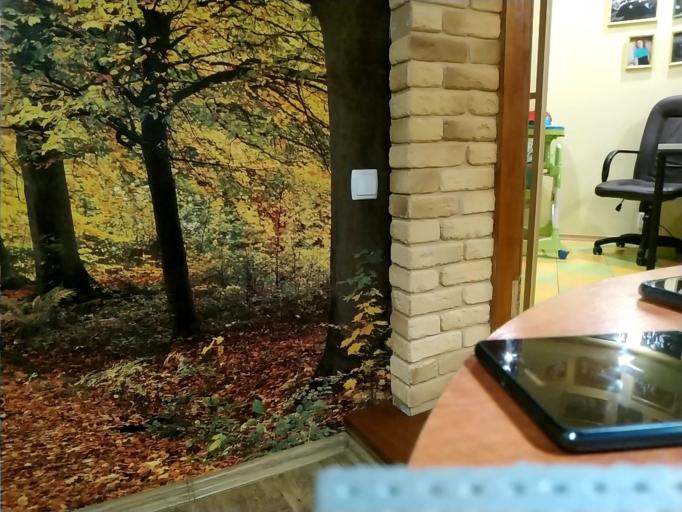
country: RU
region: Tverskaya
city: Zubtsov
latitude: 56.2225
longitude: 34.7100
